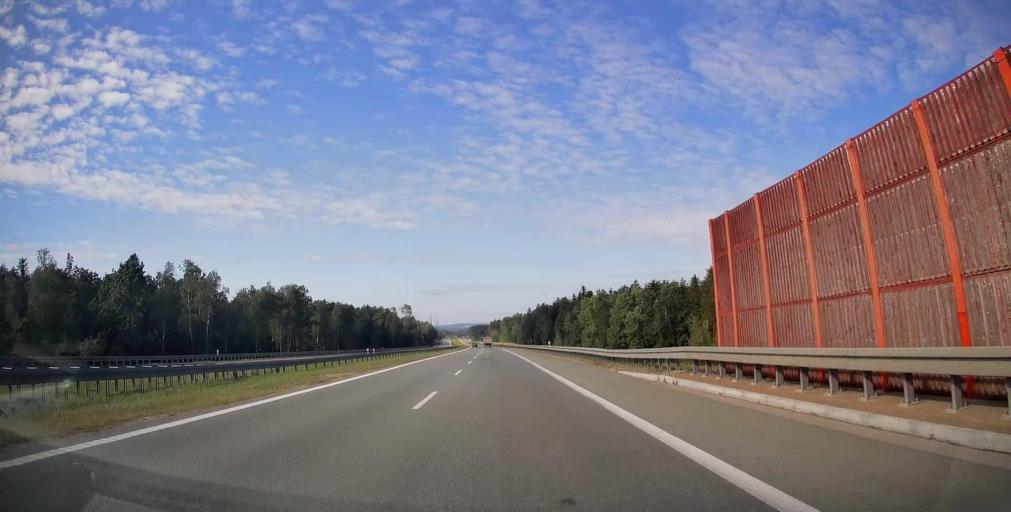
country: PL
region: Swietokrzyskie
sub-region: Powiat kielecki
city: Kostomloty Pierwsze
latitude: 50.9210
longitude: 20.6162
